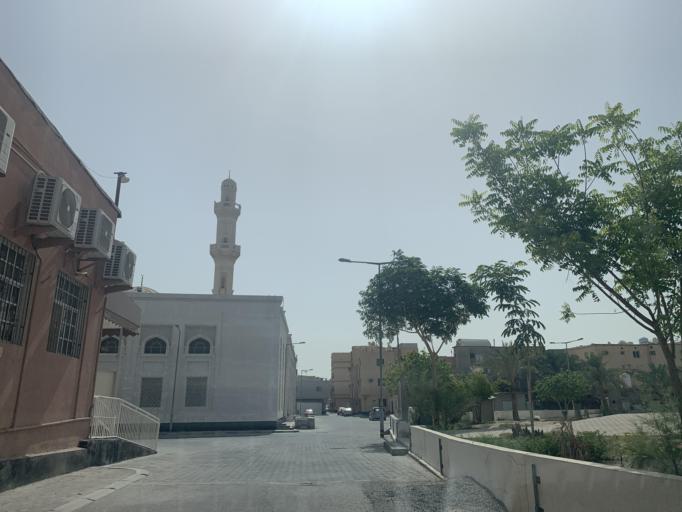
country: BH
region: Northern
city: Sitrah
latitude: 26.1607
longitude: 50.6072
